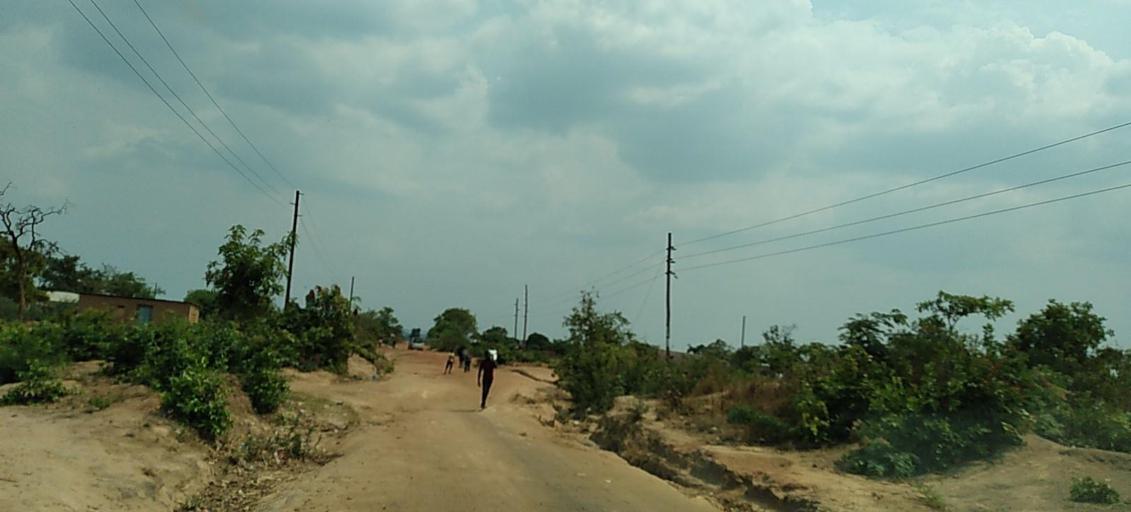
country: ZM
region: Copperbelt
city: Kalulushi
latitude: -12.8622
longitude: 28.0780
